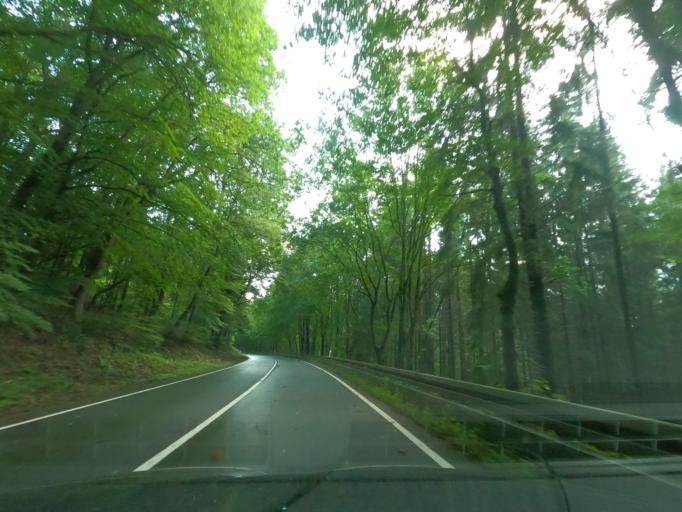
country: DE
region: North Rhine-Westphalia
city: Plettenberg
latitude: 51.2384
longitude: 7.9105
